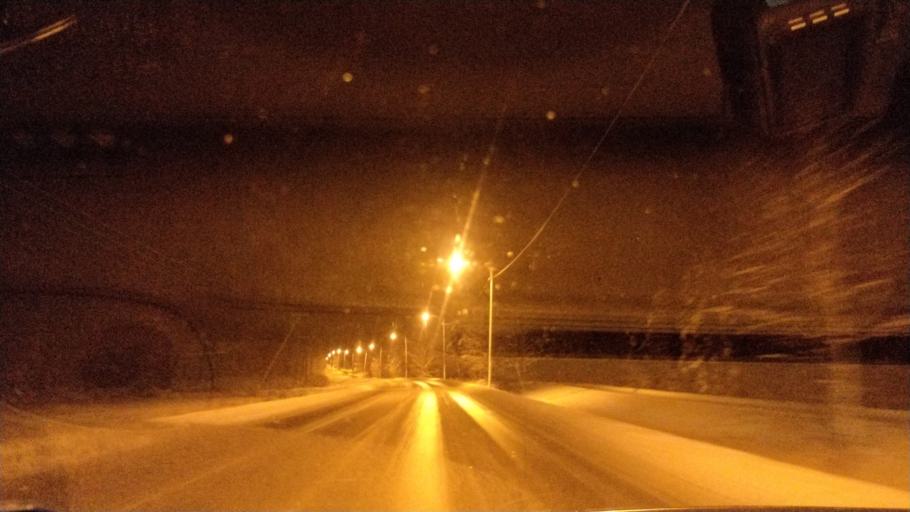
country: FI
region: Lapland
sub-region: Rovaniemi
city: Rovaniemi
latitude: 66.3025
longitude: 25.3549
